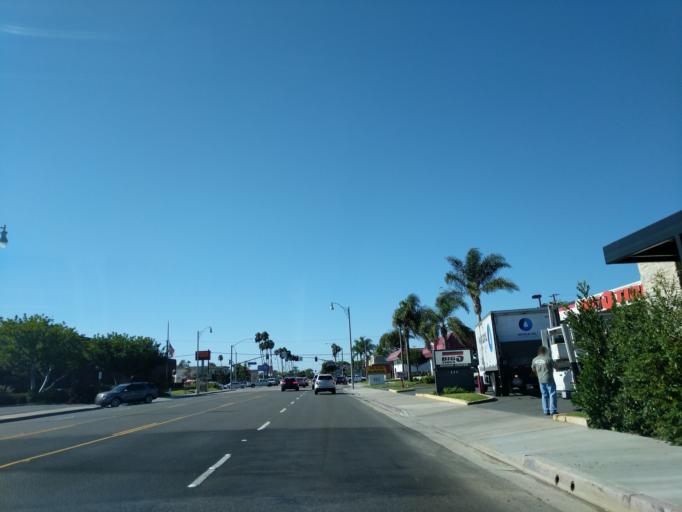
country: US
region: California
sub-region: Orange County
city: Costa Mesa
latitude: 33.6324
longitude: -117.9143
